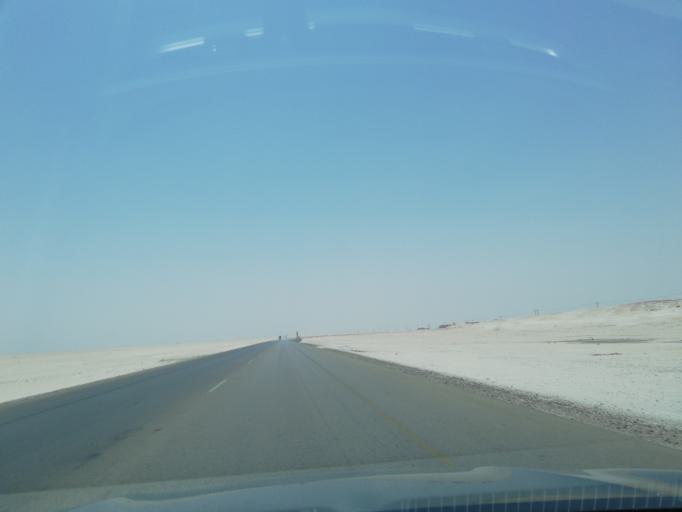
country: OM
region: Al Wusta
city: Hayma'
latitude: 20.0021
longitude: 56.3448
